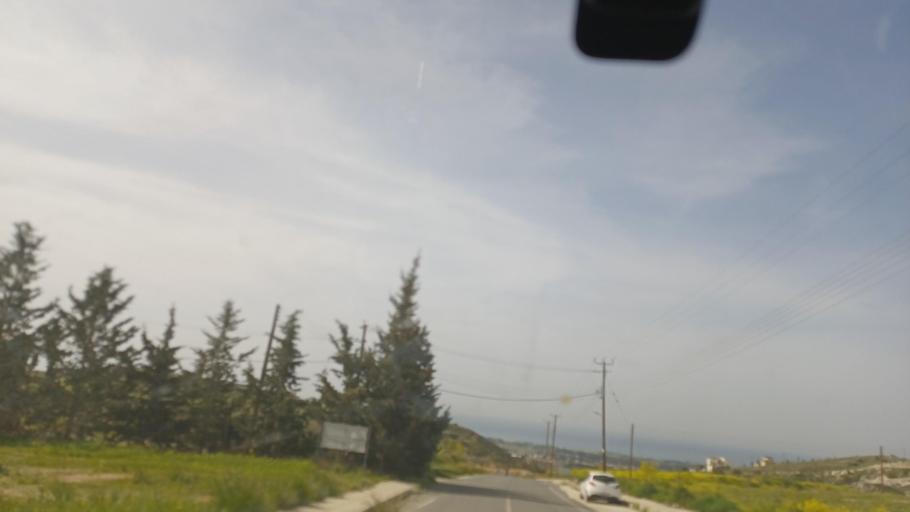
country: CY
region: Pafos
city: Mesogi
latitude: 34.7669
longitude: 32.4777
